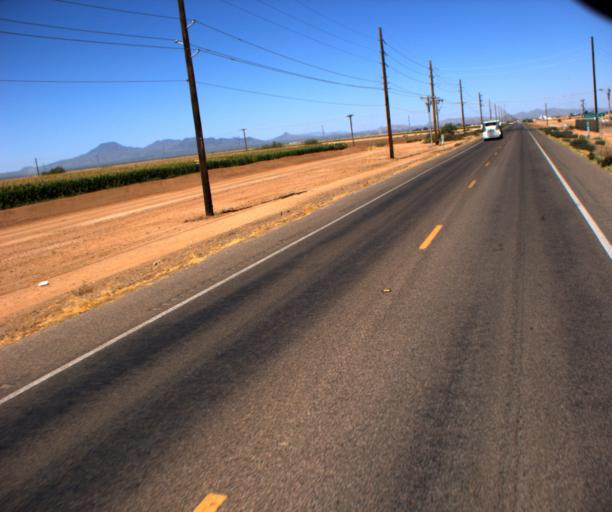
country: US
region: Arizona
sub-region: Pinal County
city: Casa Grande
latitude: 32.8794
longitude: -111.9274
